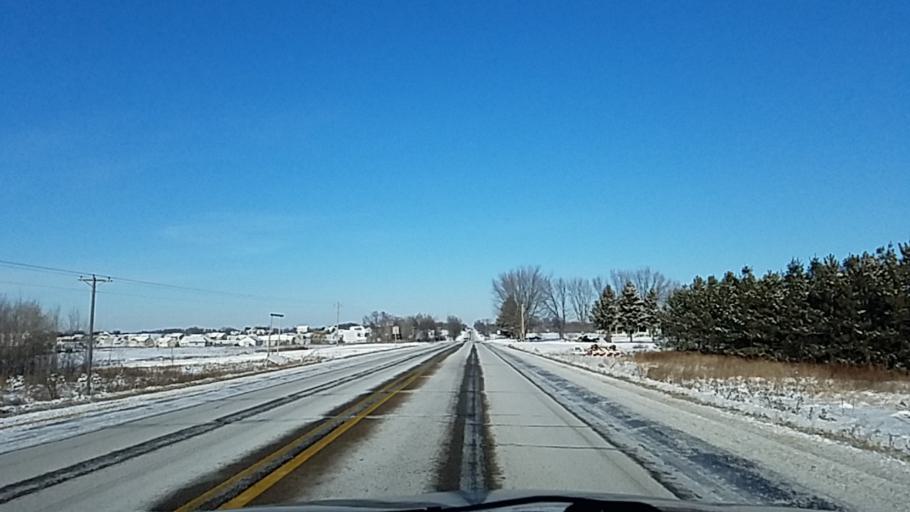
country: US
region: Wisconsin
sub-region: Saint Croix County
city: New Richmond
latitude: 45.0634
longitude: -92.5373
